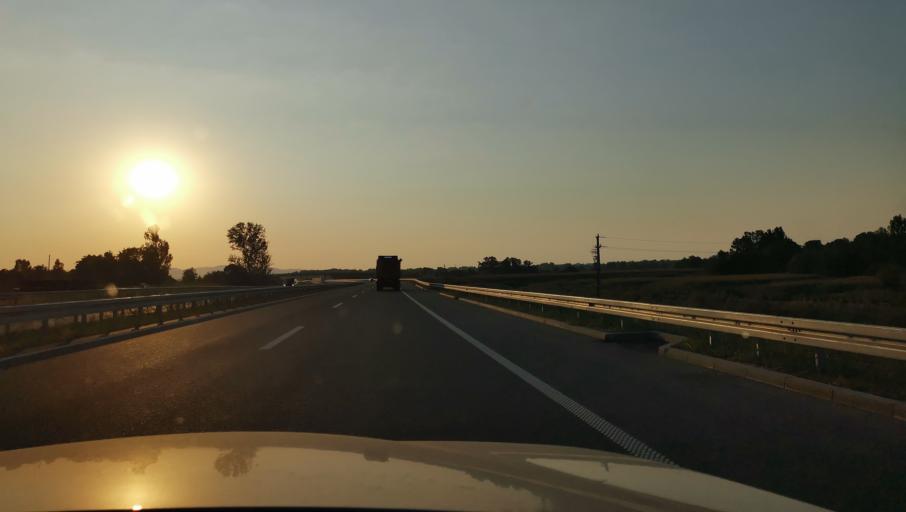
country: RS
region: Central Serbia
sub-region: Kolubarski Okrug
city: Lajkovac
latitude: 44.3449
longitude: 20.1836
